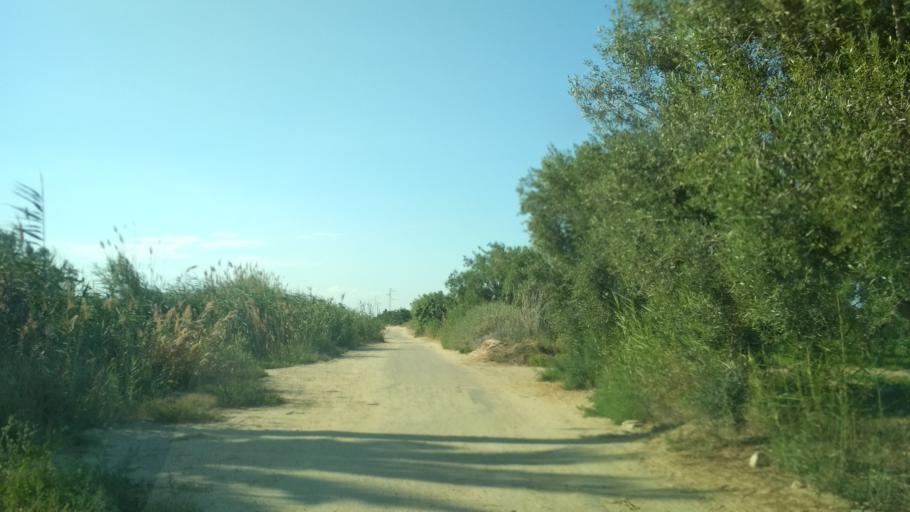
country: TN
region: Qabis
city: Gabes
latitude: 33.9579
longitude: 10.0586
